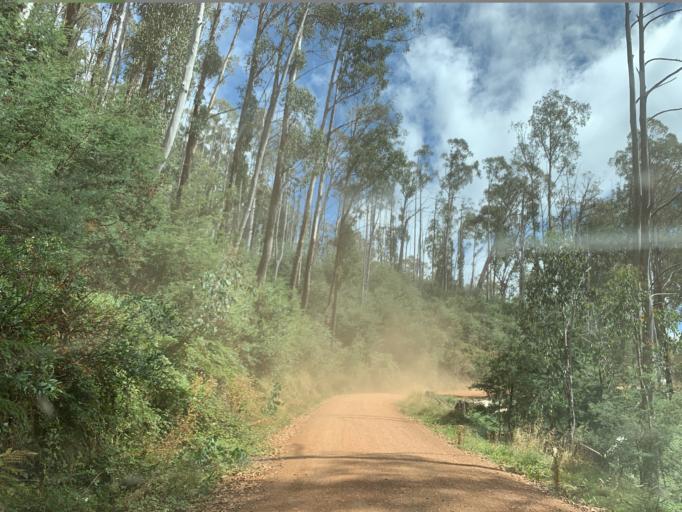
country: AU
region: Victoria
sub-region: Mansfield
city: Mansfield
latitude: -37.0971
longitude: 146.5368
